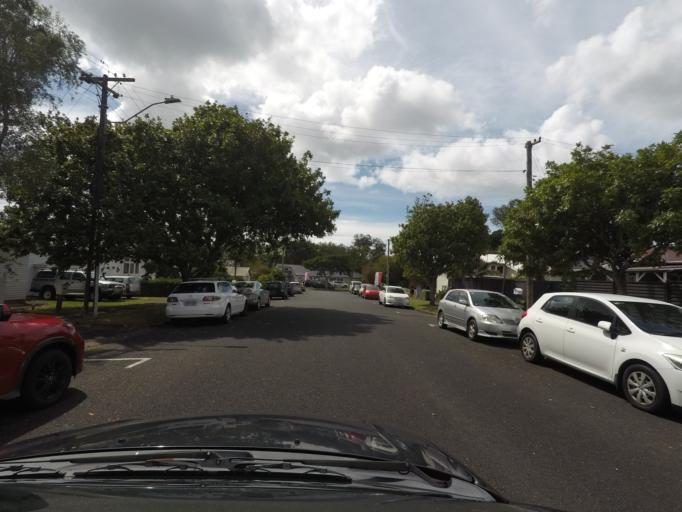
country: NZ
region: Auckland
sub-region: Auckland
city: Rosebank
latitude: -36.8829
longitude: 174.7094
